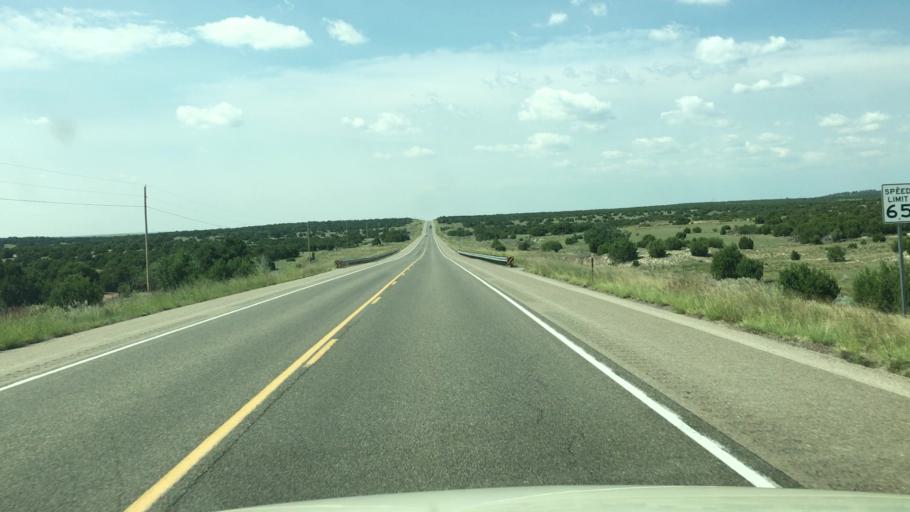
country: US
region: New Mexico
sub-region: Torrance County
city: Moriarty
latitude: 35.0462
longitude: -105.6854
